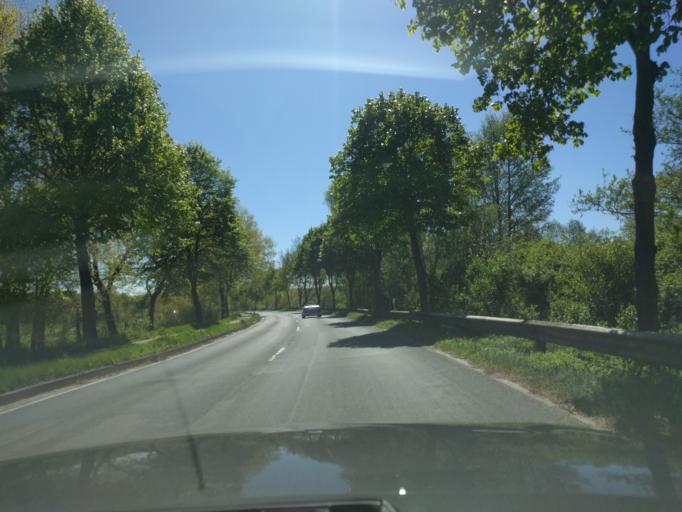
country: DE
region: Lower Saxony
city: Seevetal
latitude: 53.3905
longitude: 10.0145
